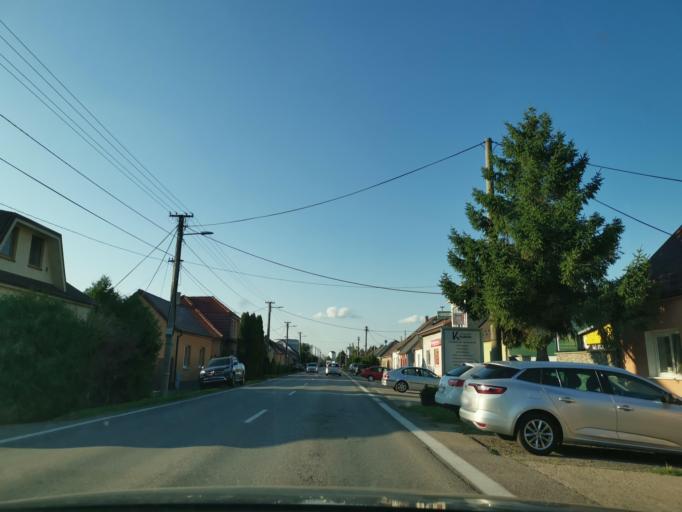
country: SK
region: Bratislavsky
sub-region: Okres Malacky
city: Malacky
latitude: 48.4225
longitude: 17.0203
